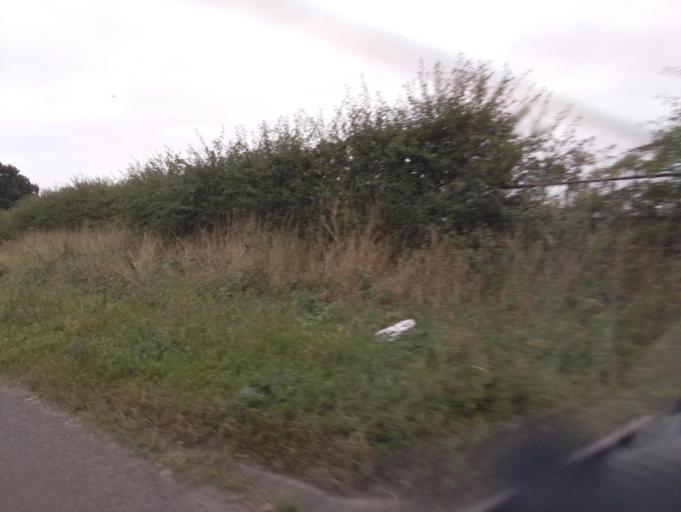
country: GB
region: England
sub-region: Shropshire
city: Shawbury
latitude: 52.7968
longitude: -2.6310
